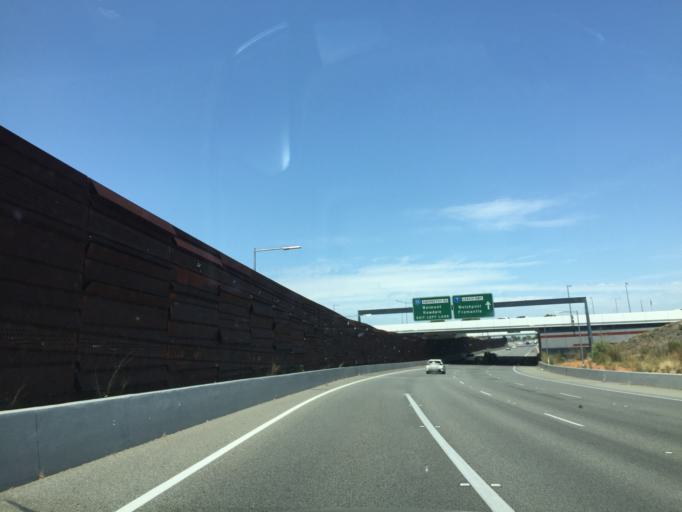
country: AU
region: Western Australia
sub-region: Belmont
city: Kewdale
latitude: -31.9661
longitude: 115.9560
